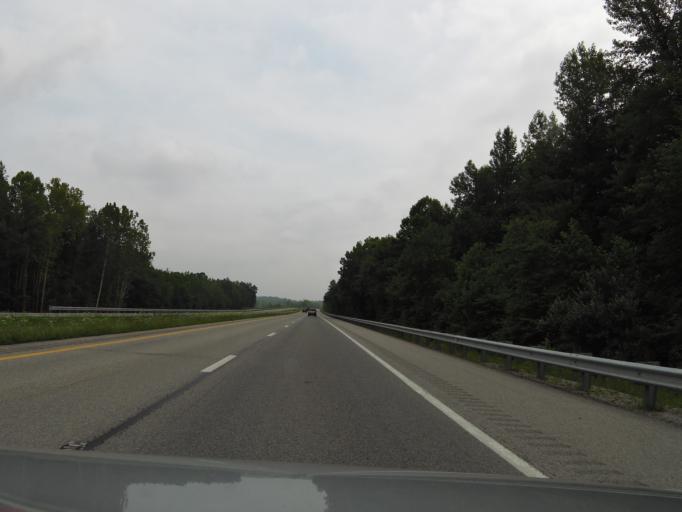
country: US
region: Kentucky
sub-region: Ohio County
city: Beaver Dam
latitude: 37.3434
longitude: -86.9367
